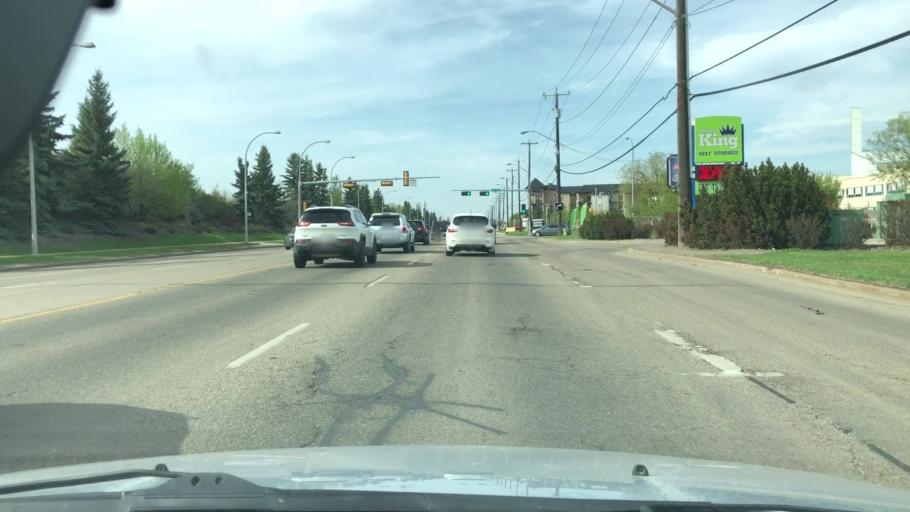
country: CA
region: Alberta
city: Edmonton
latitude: 53.6057
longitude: -113.5412
